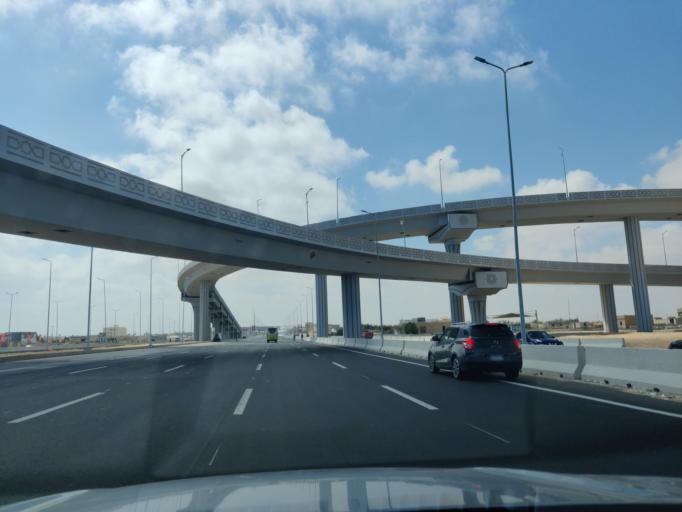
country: EG
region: Muhafazat Matruh
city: Al `Alamayn
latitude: 30.9521
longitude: 28.7705
